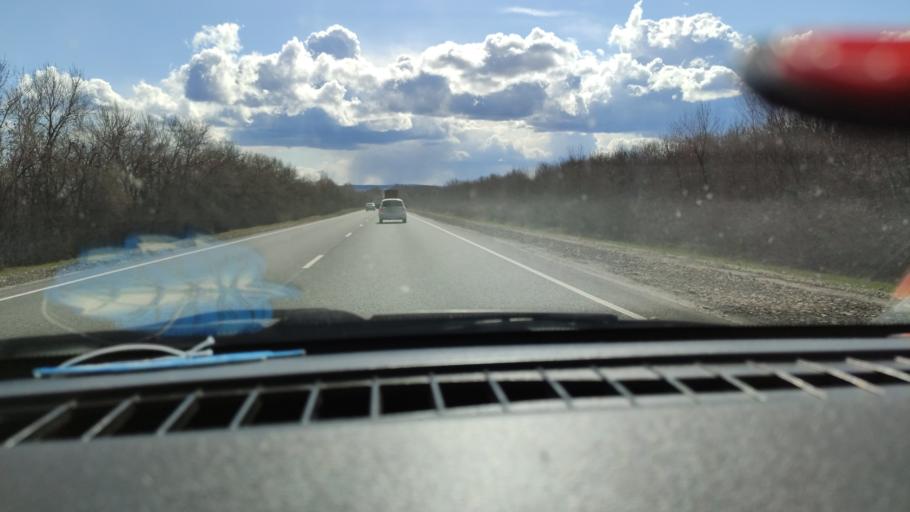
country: RU
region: Saratov
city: Khvalynsk
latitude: 52.6113
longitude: 48.1594
